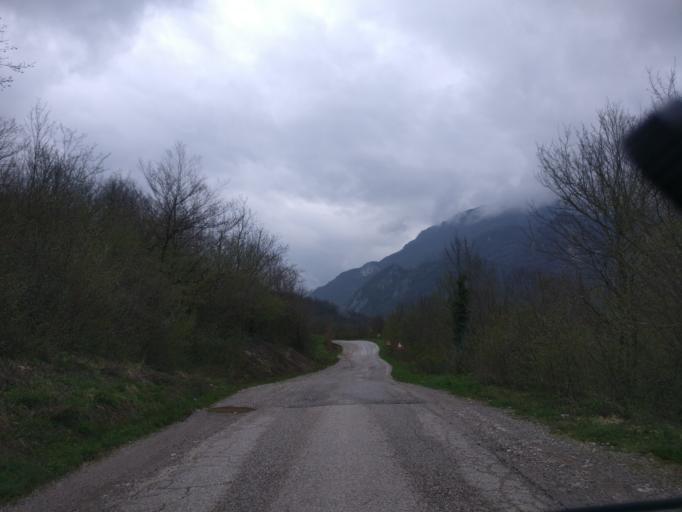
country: BA
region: Republika Srpska
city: Foca
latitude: 43.3517
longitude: 18.8291
